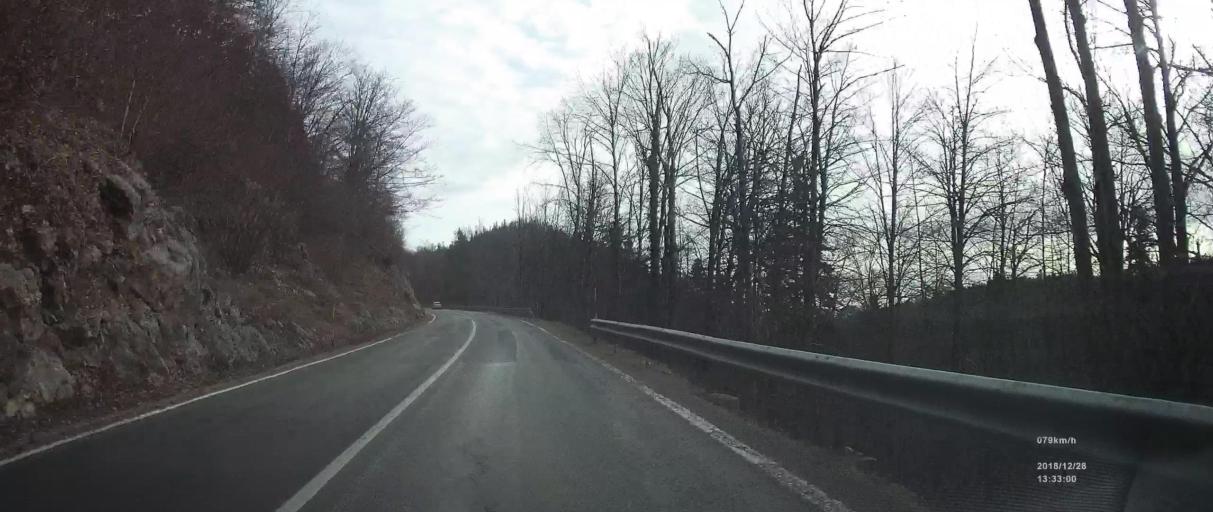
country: HR
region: Primorsko-Goranska
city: Hreljin
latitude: 45.3420
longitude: 14.6715
